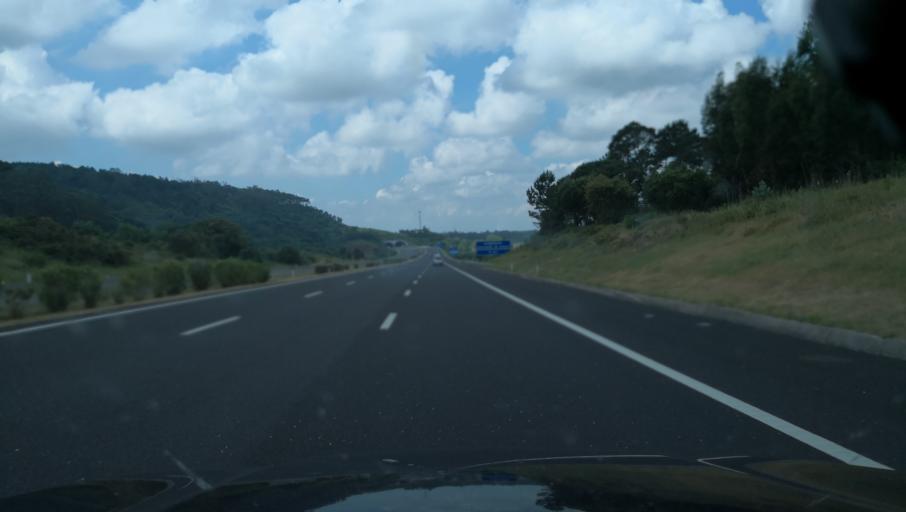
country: PT
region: Leiria
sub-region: Caldas da Rainha
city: Caldas da Rainha
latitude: 39.4695
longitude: -9.1100
